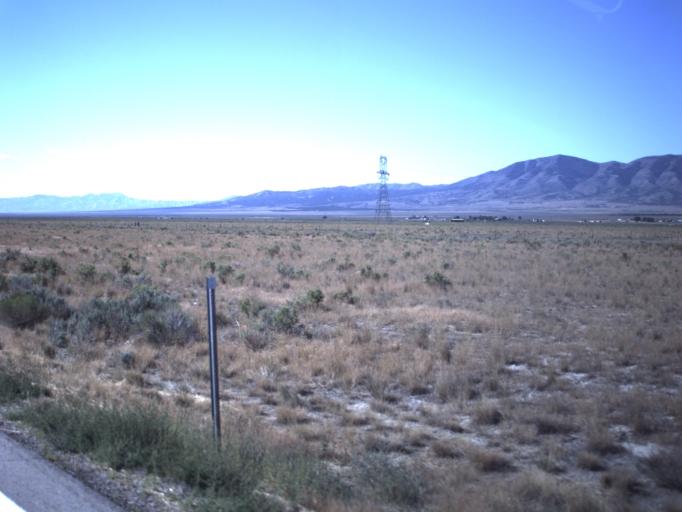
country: US
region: Utah
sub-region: Tooele County
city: Tooele
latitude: 40.3569
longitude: -112.4134
